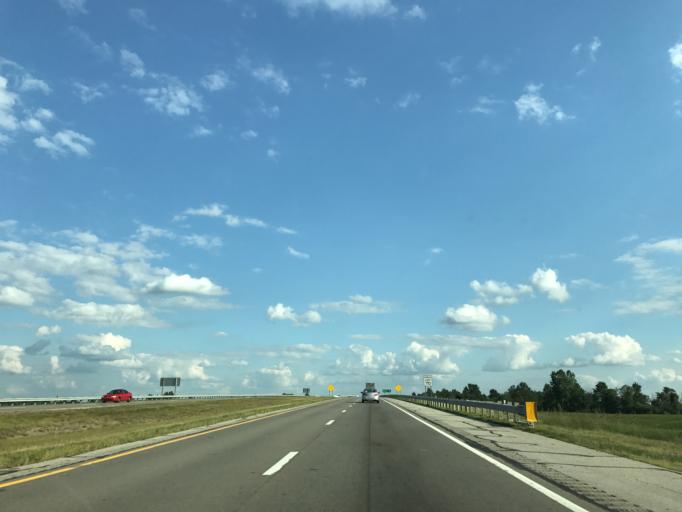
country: US
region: Ohio
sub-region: Crawford County
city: Bucyrus
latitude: 40.8048
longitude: -82.9249
